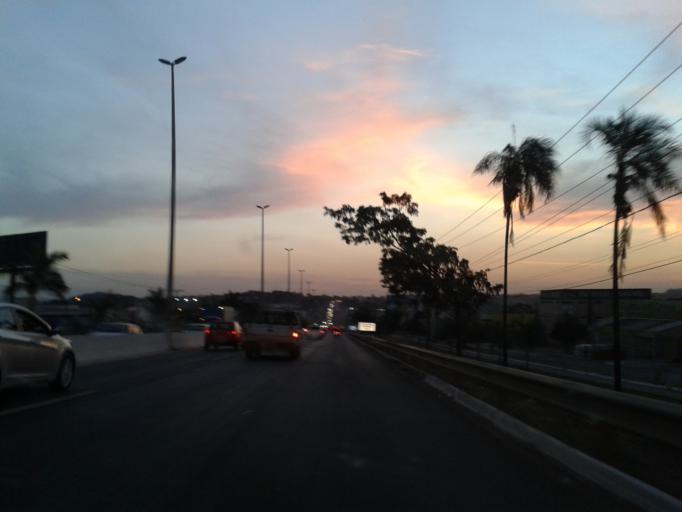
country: BR
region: Goias
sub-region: Goiania
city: Goiania
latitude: -16.6596
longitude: -49.3512
